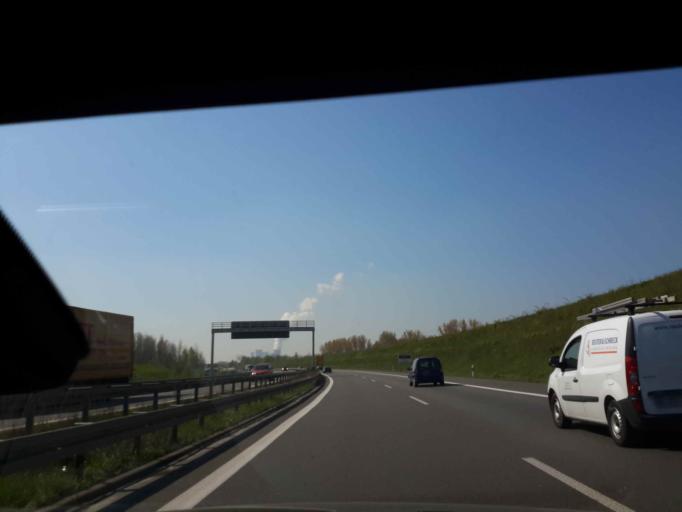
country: DE
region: Saxony
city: Bohlen
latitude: 51.2380
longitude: 12.3898
